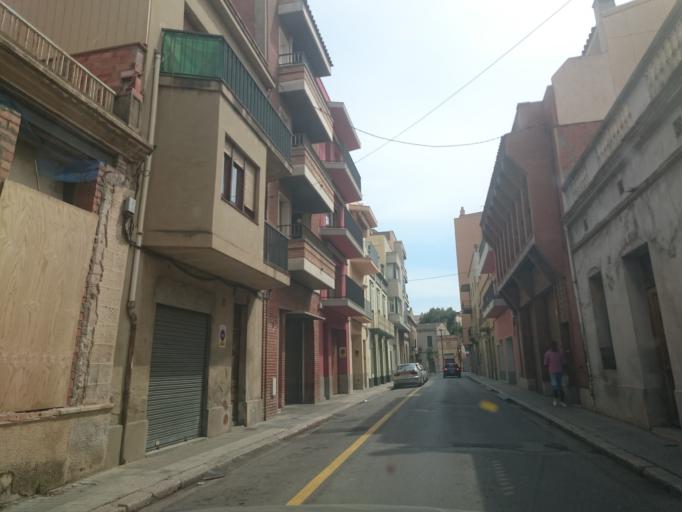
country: ES
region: Catalonia
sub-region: Provincia de Girona
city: Figueres
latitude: 42.2672
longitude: 2.9675
